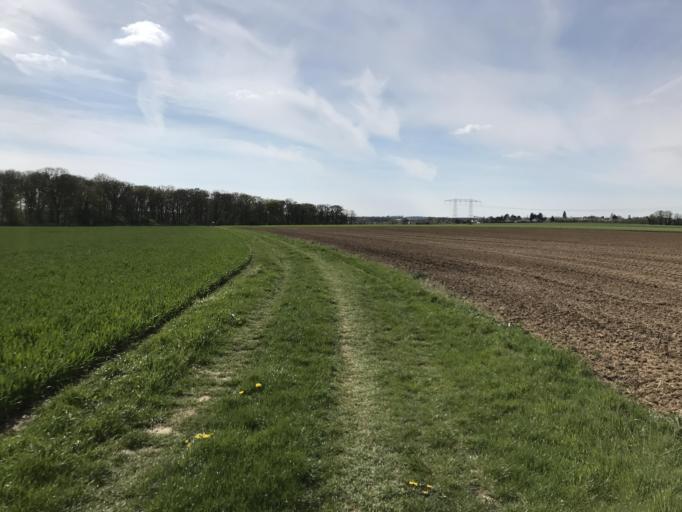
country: FR
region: Ile-de-France
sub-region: Departement de l'Essonne
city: Gometz-le-Chatel
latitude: 48.6674
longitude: 2.1451
